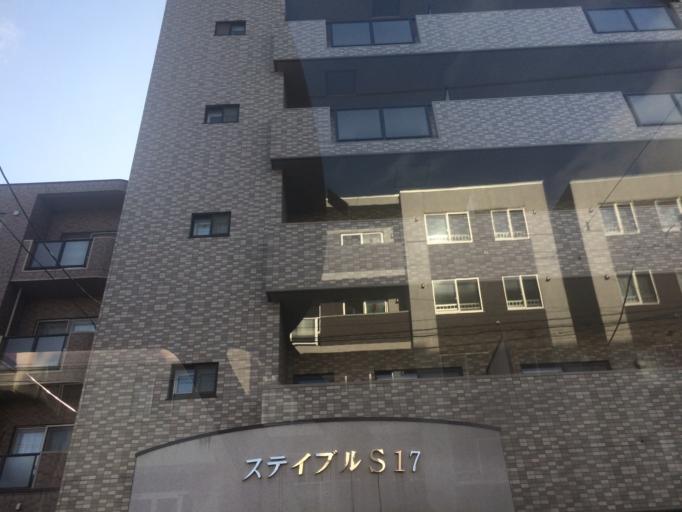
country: JP
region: Hokkaido
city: Sapporo
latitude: 43.0377
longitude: 141.3511
